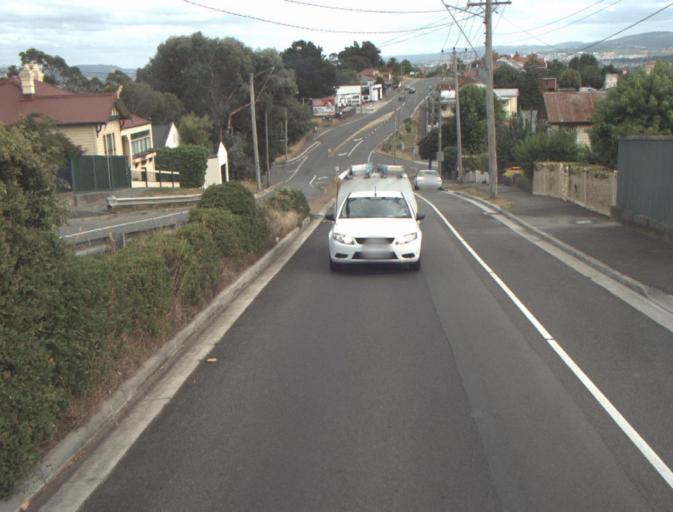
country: AU
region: Tasmania
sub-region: Launceston
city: East Launceston
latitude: -41.4495
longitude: 147.1532
